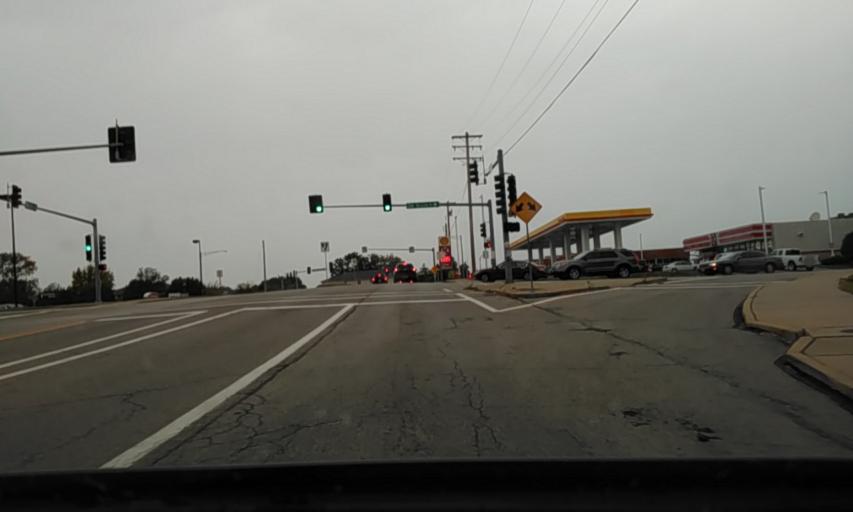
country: US
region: Missouri
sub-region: Saint Louis County
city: Concord
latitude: 38.5096
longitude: -90.3732
